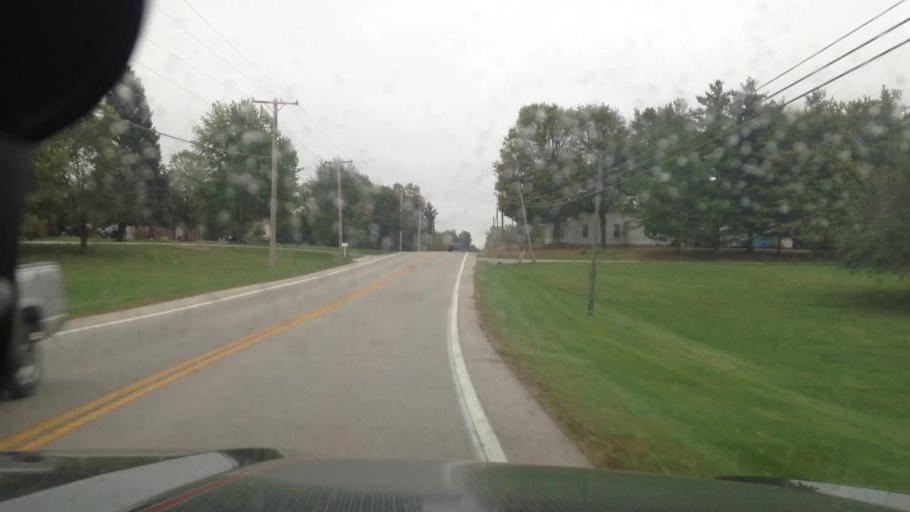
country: US
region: Ohio
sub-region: Darke County
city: Greenville
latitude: 40.1319
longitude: -84.6940
